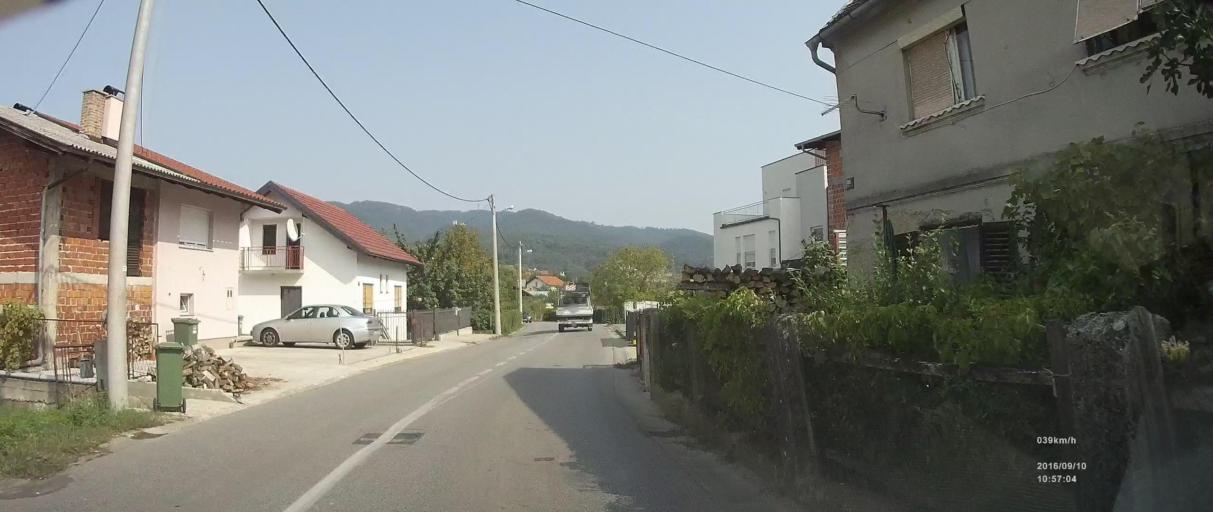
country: HR
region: Grad Zagreb
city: Zagreb
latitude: 45.8397
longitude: 15.9358
